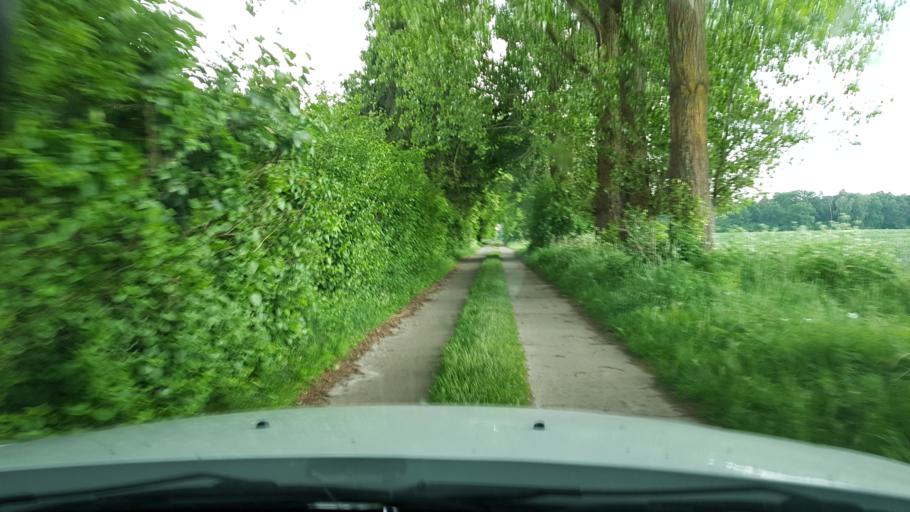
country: PL
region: West Pomeranian Voivodeship
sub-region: Powiat stargardzki
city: Stara Dabrowa
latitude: 53.3517
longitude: 15.1816
